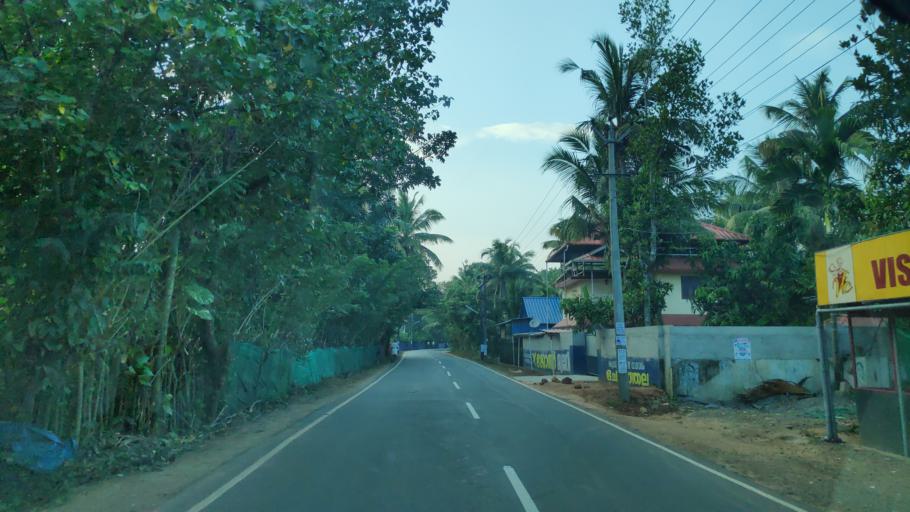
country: IN
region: Kerala
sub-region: Alappuzha
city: Shertallai
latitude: 9.6764
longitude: 76.3810
